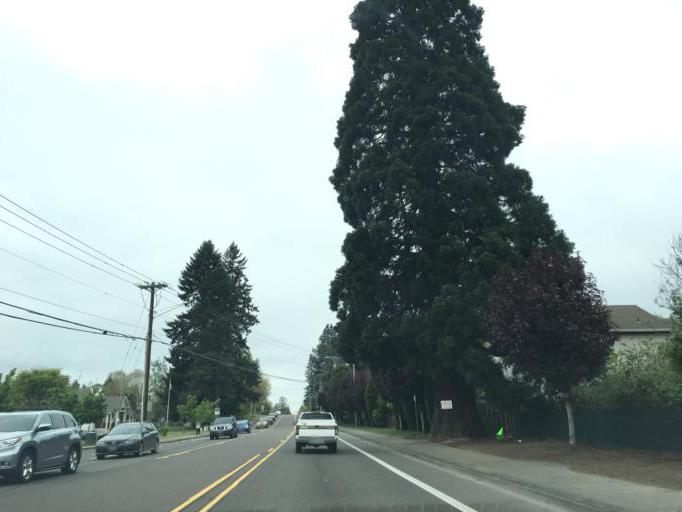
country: US
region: Oregon
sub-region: Washington County
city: Durham
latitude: 45.4043
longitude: -122.7585
